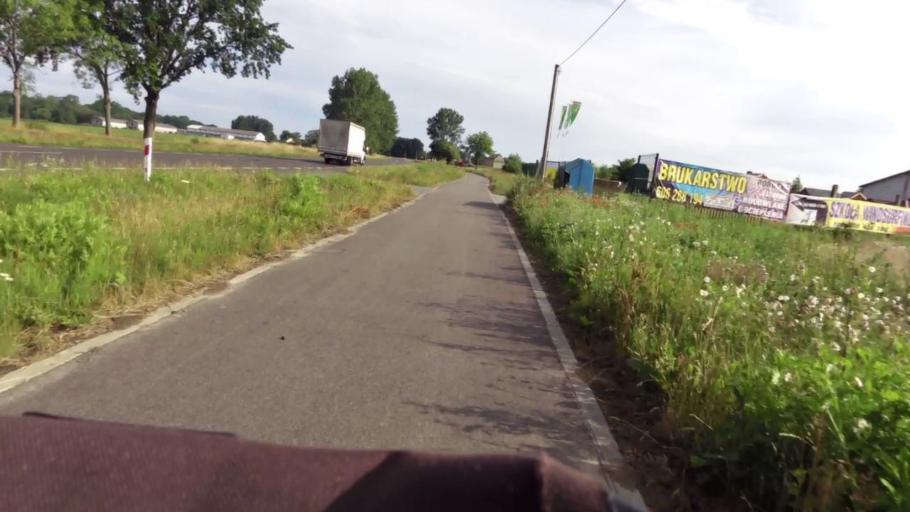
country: PL
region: West Pomeranian Voivodeship
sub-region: Powiat kamienski
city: Dziwnow
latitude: 54.0076
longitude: 14.8171
